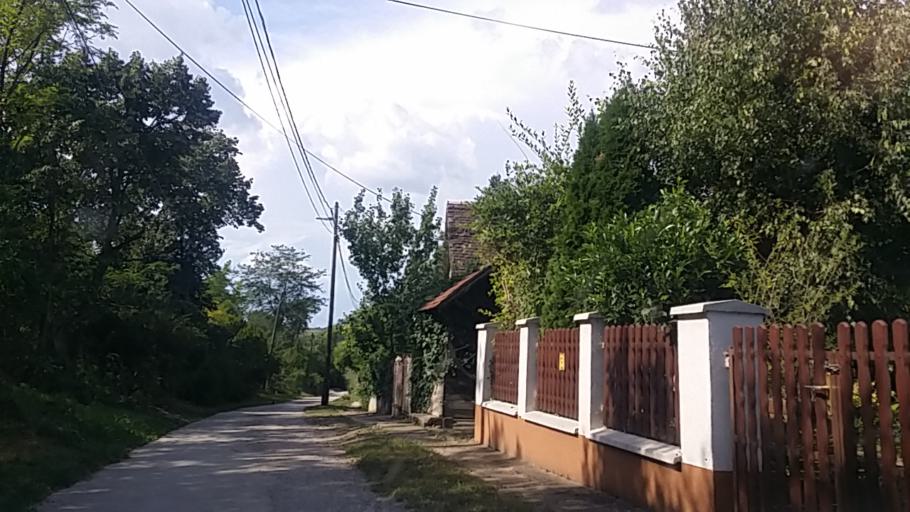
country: HU
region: Tolna
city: Gyonk
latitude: 46.5429
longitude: 18.4704
